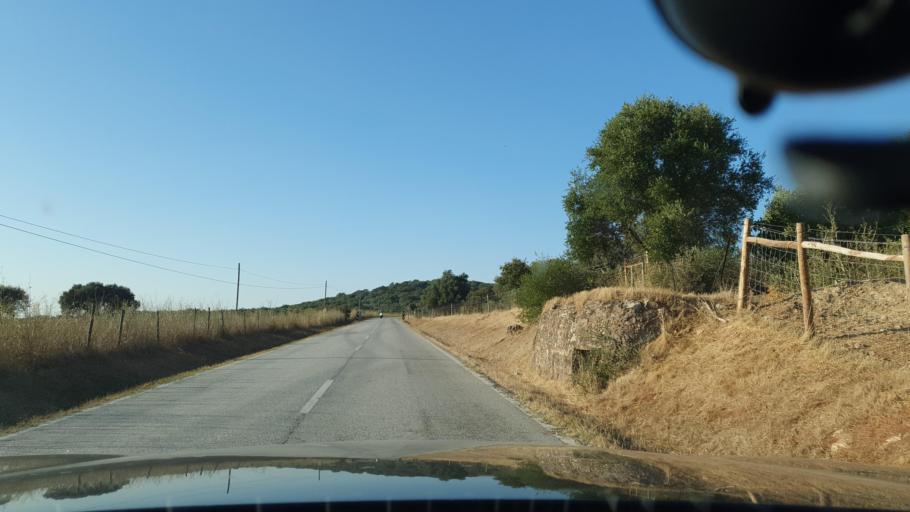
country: PT
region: Evora
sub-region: Estremoz
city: Estremoz
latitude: 38.9008
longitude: -7.6676
